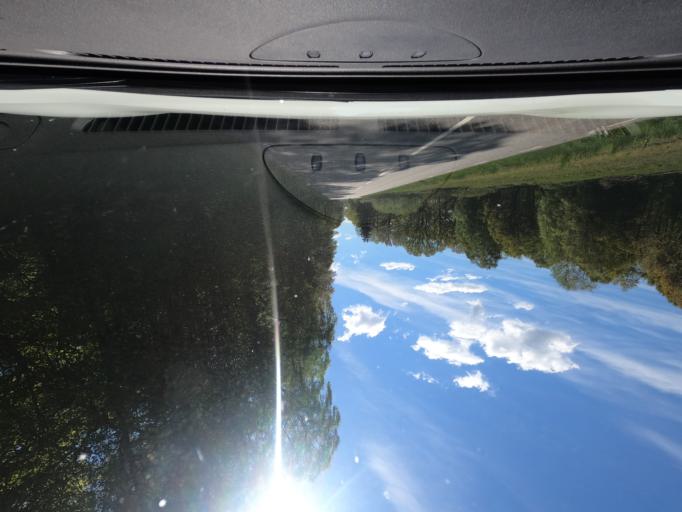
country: SE
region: Halland
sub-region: Kungsbacka Kommun
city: Fjaeras kyrkby
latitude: 57.4342
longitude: 12.1814
